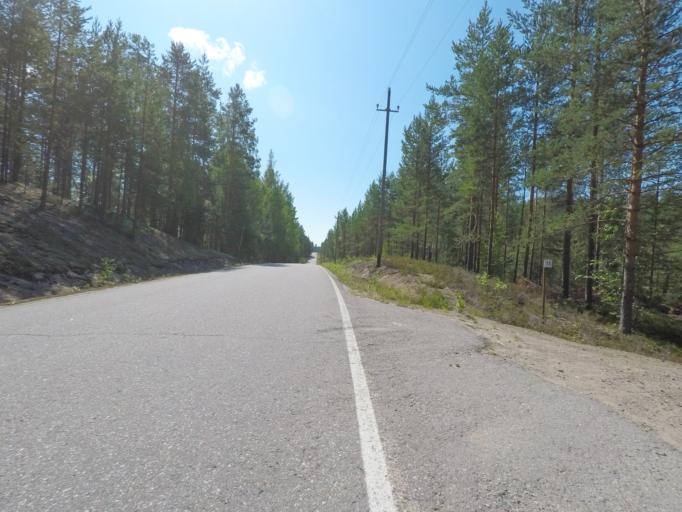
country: FI
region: Southern Savonia
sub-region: Mikkeli
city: Puumala
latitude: 61.4596
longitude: 28.1751
